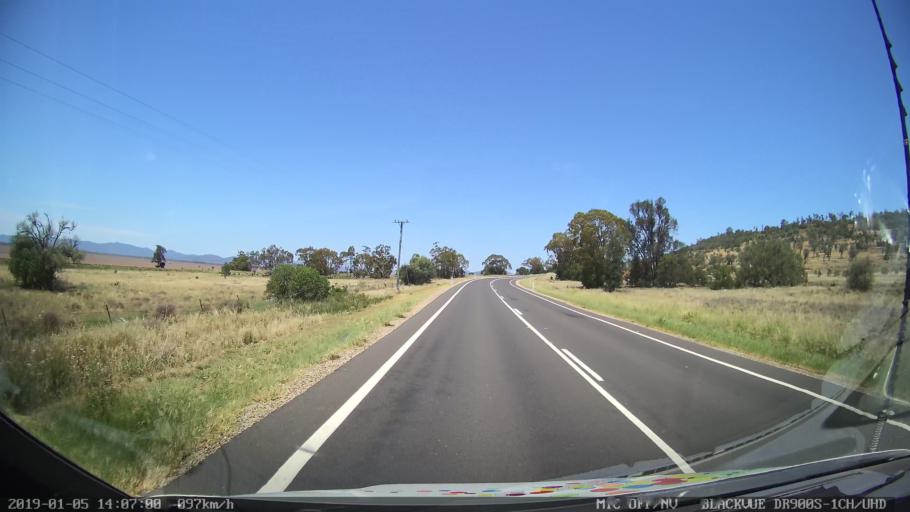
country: AU
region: New South Wales
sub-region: Gunnedah
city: Gunnedah
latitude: -31.2190
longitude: 150.4006
